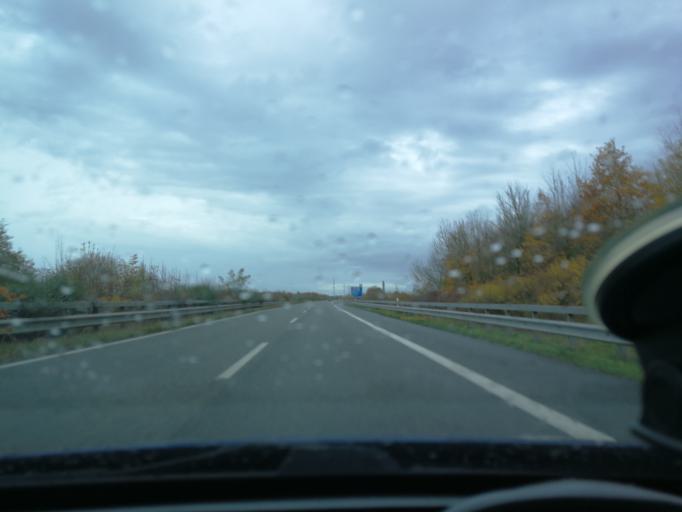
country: DE
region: Rheinland-Pfalz
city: Trierweiler
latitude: 49.7570
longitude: 6.5727
